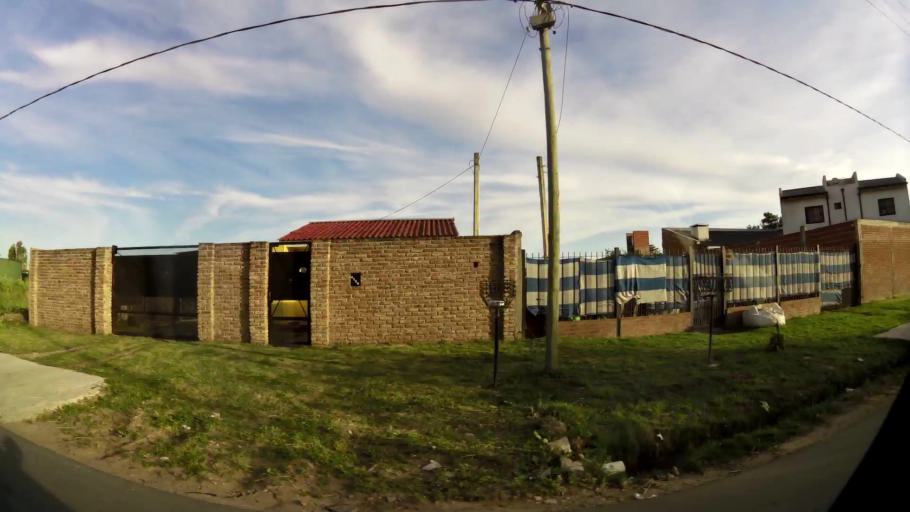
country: AR
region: Buenos Aires
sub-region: Partido de Almirante Brown
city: Adrogue
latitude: -34.7909
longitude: -58.3444
